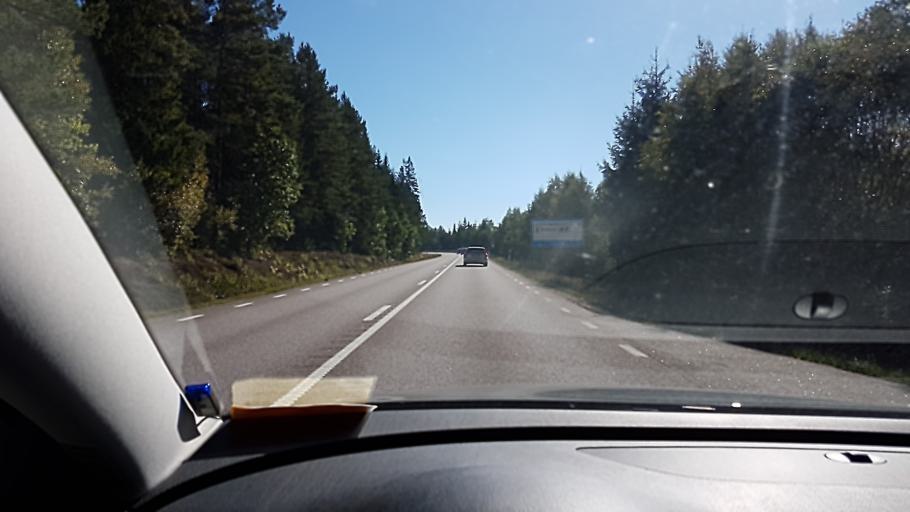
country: SE
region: Kronoberg
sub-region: Lessebo Kommun
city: Hovmantorp
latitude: 56.7825
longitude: 15.1986
